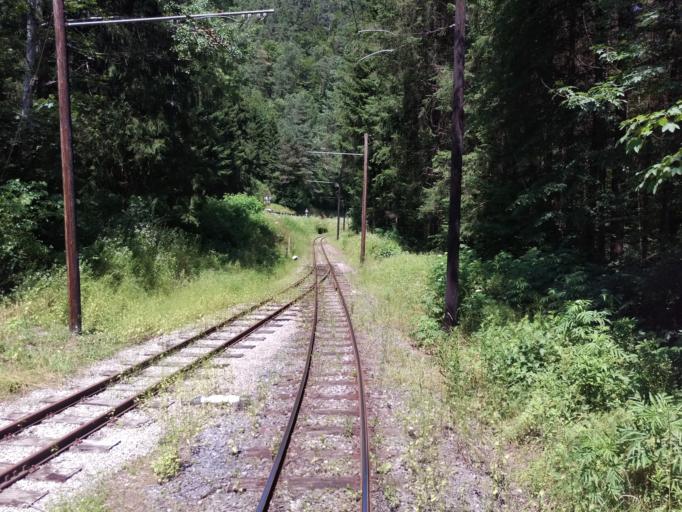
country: AT
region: Styria
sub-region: Politischer Bezirk Bruck-Muerzzuschlag
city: Pernegg an der Mur
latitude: 47.3681
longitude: 15.3828
